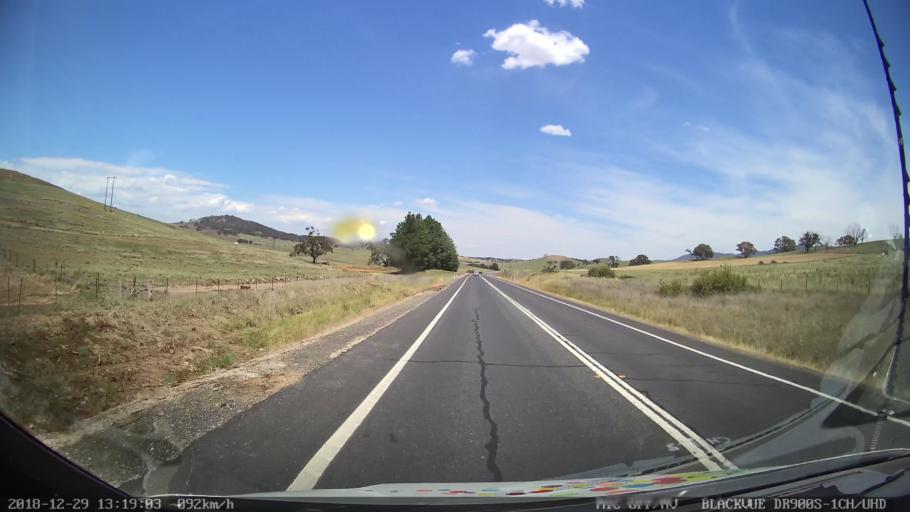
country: AU
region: Australian Capital Territory
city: Macarthur
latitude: -35.7596
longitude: 149.1613
